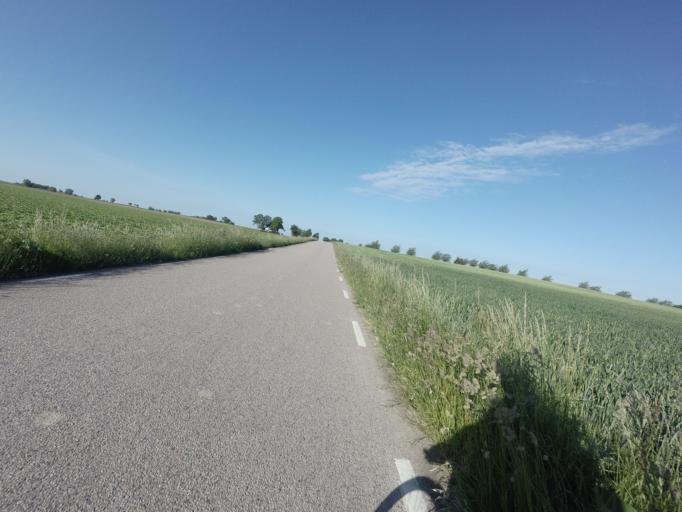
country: SE
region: Skane
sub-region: Malmo
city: Oxie
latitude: 55.4622
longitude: 13.1277
